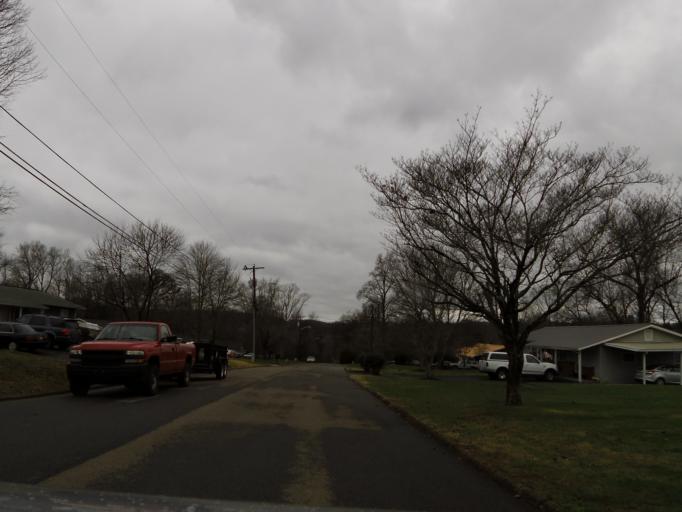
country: US
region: Tennessee
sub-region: Knox County
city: Knoxville
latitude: 35.9779
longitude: -84.0009
